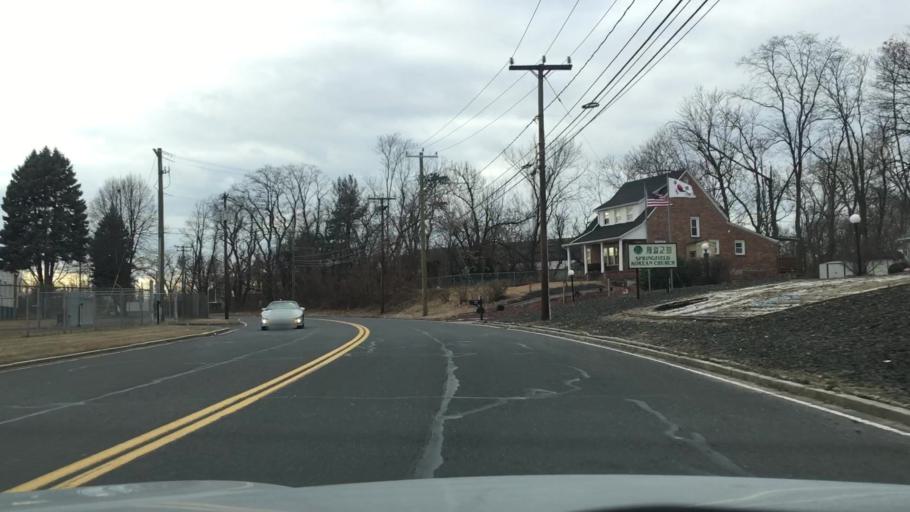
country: US
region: Massachusetts
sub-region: Hampden County
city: Springfield
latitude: 42.1443
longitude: -72.5453
